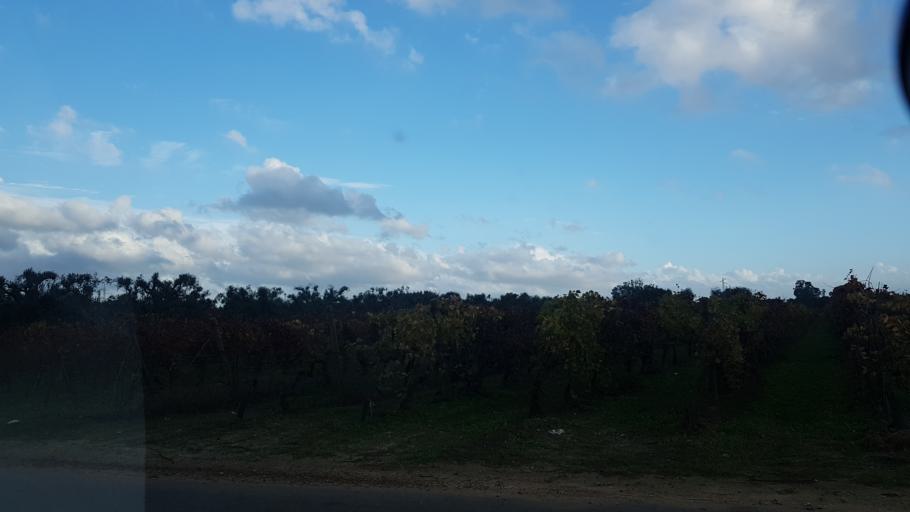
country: IT
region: Apulia
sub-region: Provincia di Brindisi
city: San Pietro Vernotico
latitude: 40.5090
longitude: 18.0207
